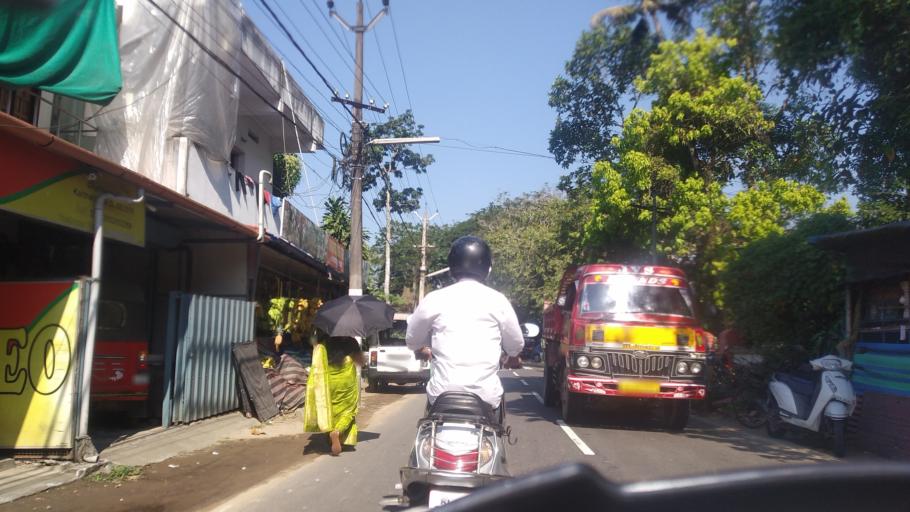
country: IN
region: Kerala
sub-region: Ernakulam
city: Elur
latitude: 10.1221
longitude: 76.2457
